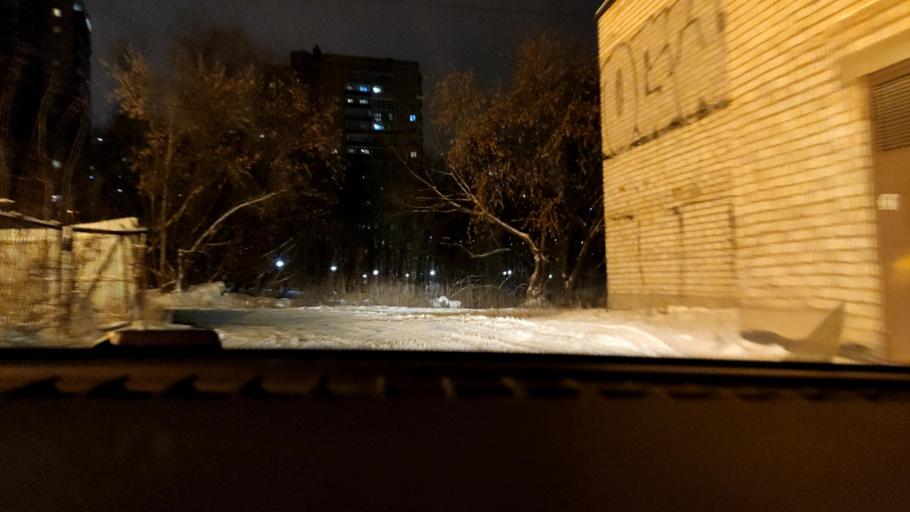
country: RU
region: Samara
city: Samara
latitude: 53.2466
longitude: 50.1846
